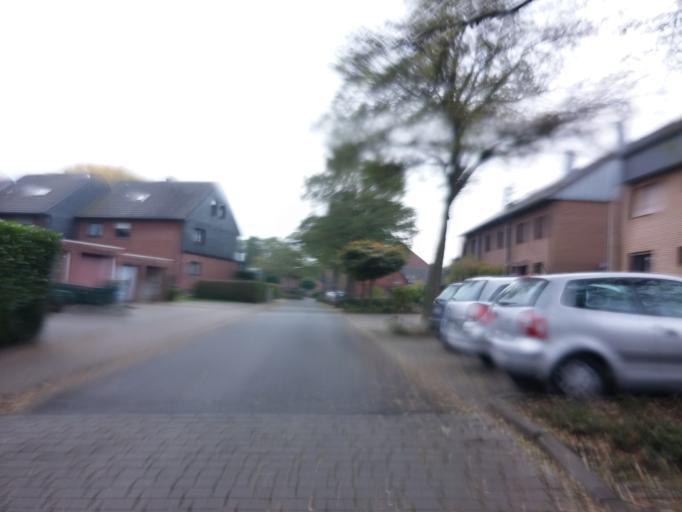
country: DE
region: North Rhine-Westphalia
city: Dorsten
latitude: 51.6627
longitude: 6.9454
